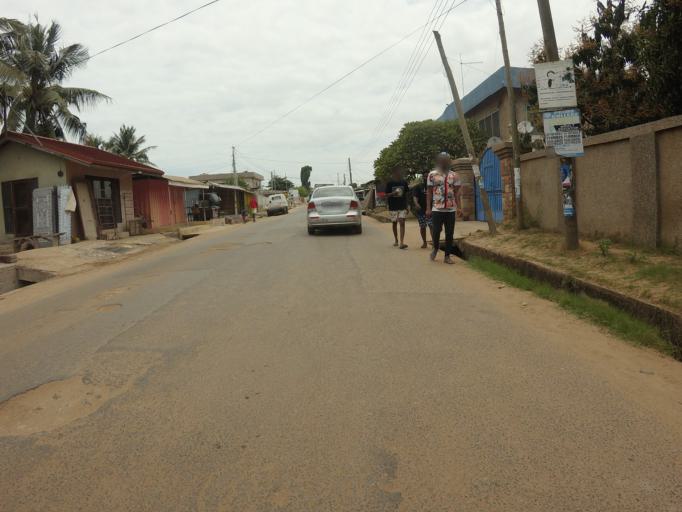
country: GH
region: Greater Accra
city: Nungua
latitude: 5.6068
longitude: -0.0965
